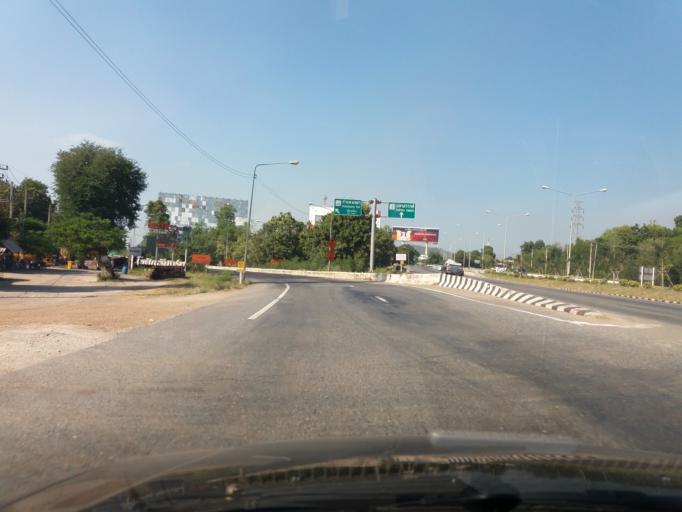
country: TH
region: Nakhon Sawan
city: Krok Phra
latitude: 15.6149
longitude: 100.1210
